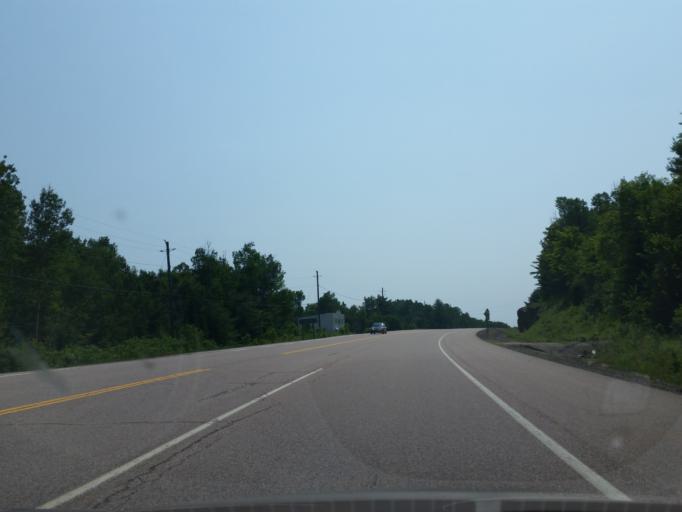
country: CA
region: Ontario
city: Deep River
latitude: 46.2126
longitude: -77.8944
